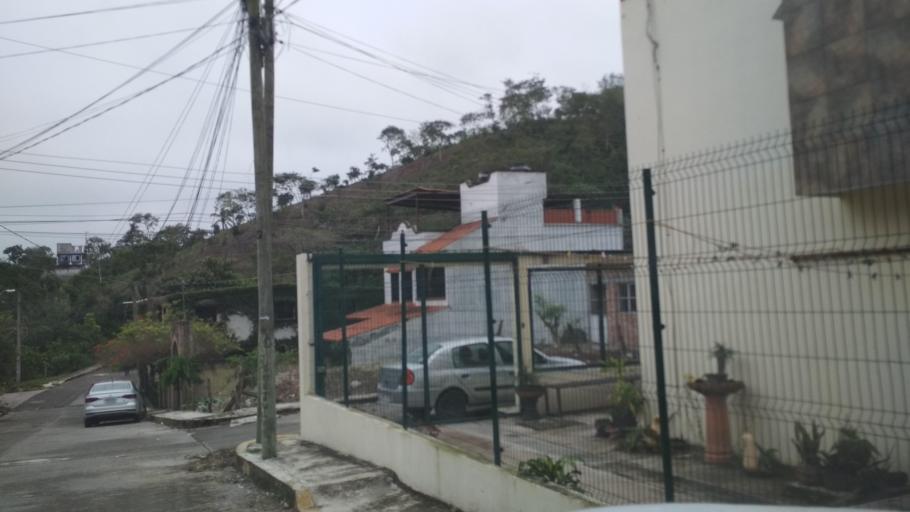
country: MX
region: Veracruz
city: Papantla de Olarte
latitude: 20.4432
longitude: -97.3099
